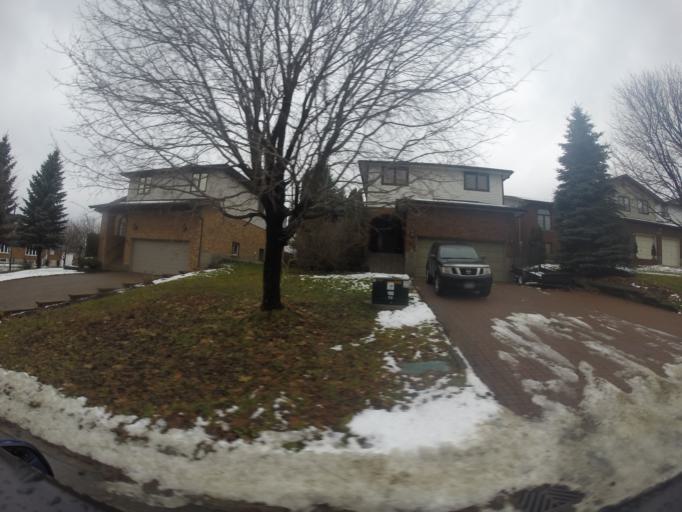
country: CA
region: Ontario
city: Greater Sudbury
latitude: 46.5260
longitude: -80.9369
